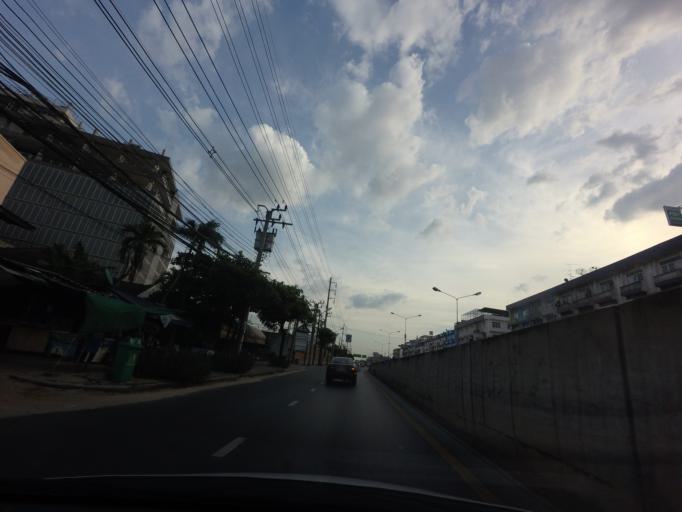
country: TH
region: Bangkok
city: Bang Khun Thian
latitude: 13.6542
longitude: 100.4305
